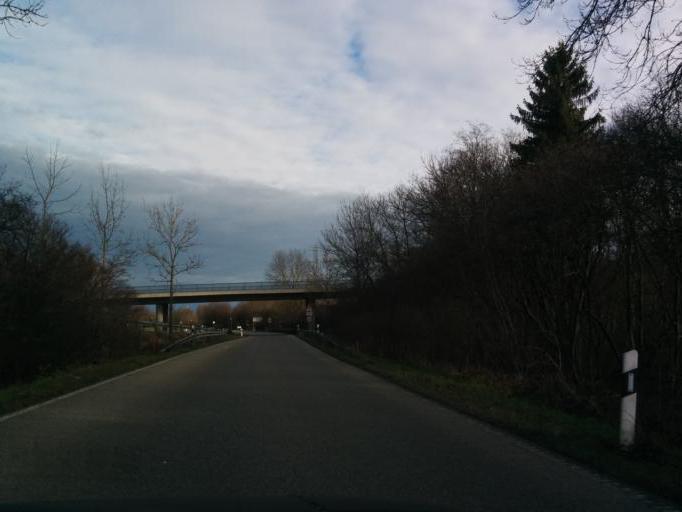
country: DE
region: Bavaria
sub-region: Upper Bavaria
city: Dachau
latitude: 48.2433
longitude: 11.4530
